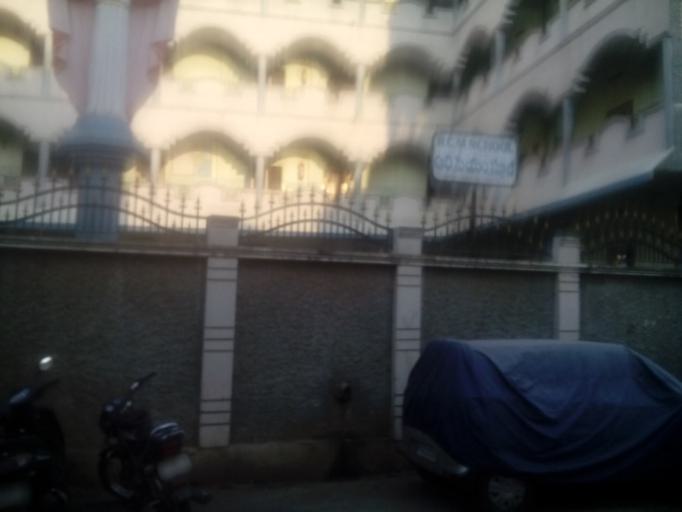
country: IN
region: Andhra Pradesh
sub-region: Krishna
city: Vijayawada
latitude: 16.5274
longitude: 80.6123
